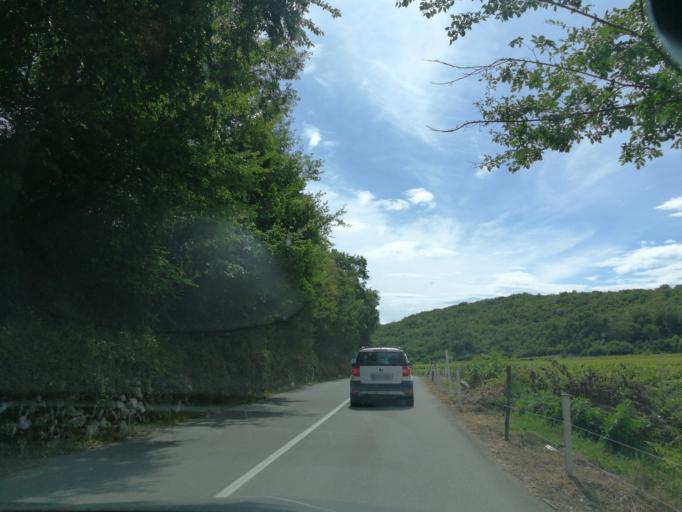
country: HR
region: Primorsko-Goranska
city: Punat
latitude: 45.0887
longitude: 14.6420
